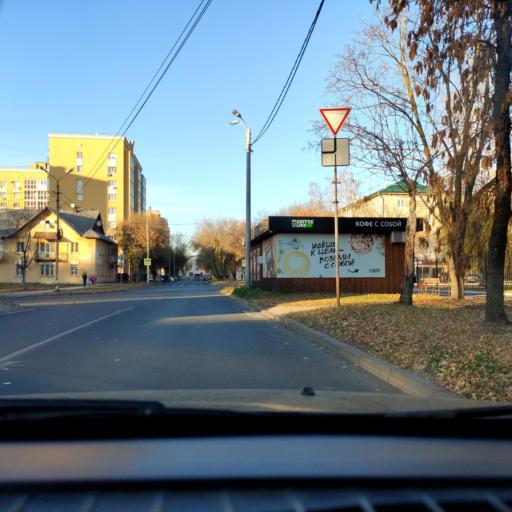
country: RU
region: Samara
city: Tol'yatti
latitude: 53.5006
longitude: 49.3964
